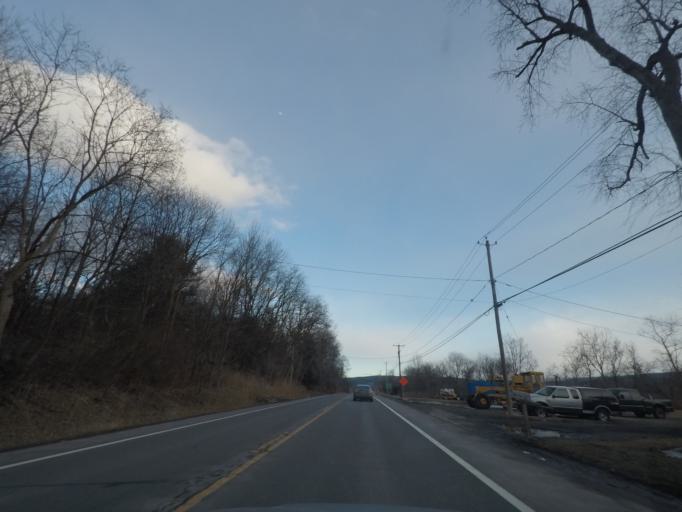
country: US
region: New York
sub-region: Herkimer County
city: Ilion
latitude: 43.0250
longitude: -75.0364
